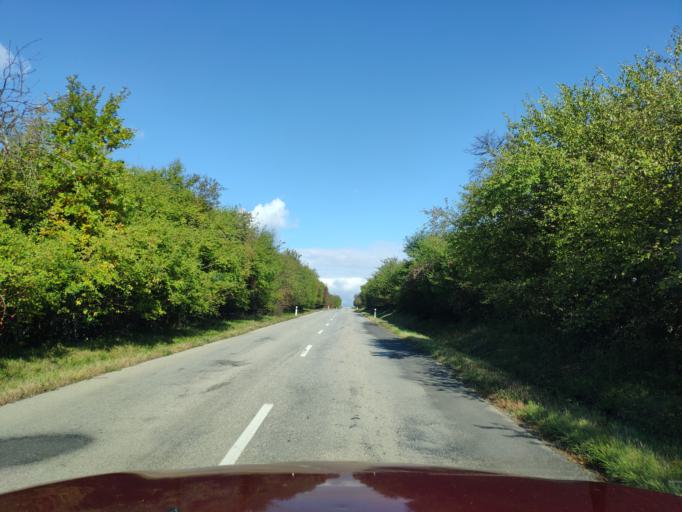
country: SK
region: Presovsky
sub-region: Okres Presov
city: Presov
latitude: 48.8915
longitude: 21.2602
